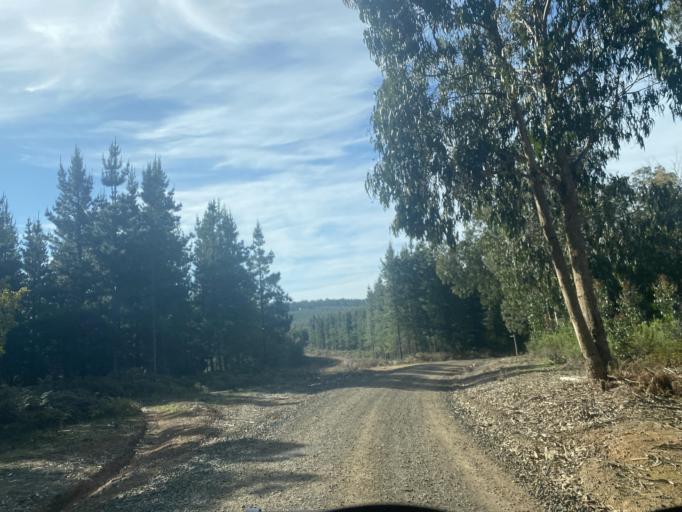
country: AU
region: Victoria
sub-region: Mansfield
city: Mansfield
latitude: -36.8702
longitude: 146.1777
